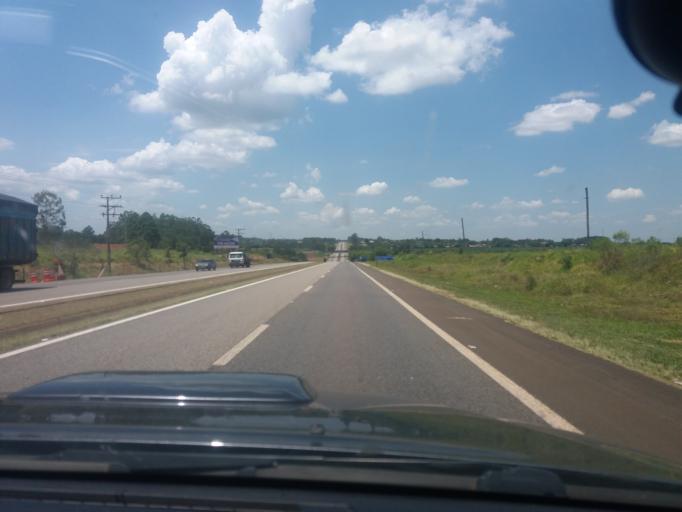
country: BR
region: Sao Paulo
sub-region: Itapetininga
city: Itapetininga
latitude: -23.5635
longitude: -47.9744
